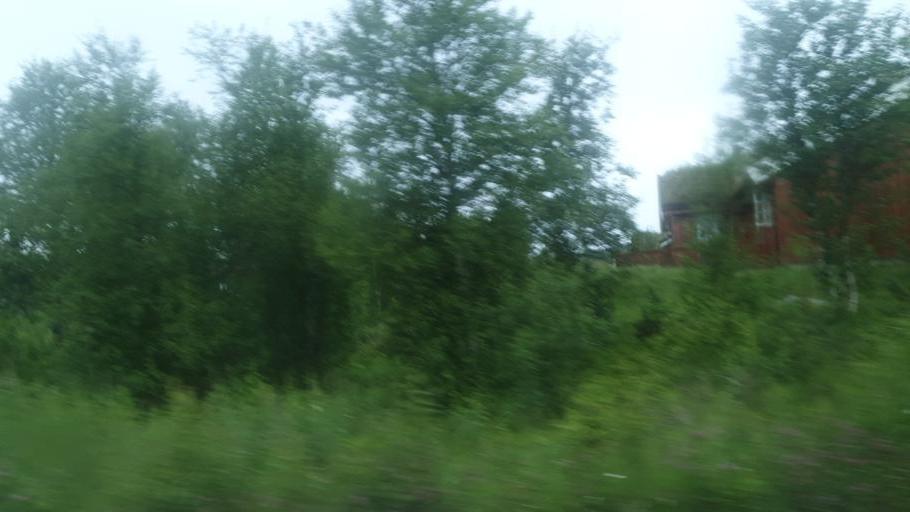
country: NO
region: Oppland
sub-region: Vestre Slidre
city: Slidre
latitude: 61.2400
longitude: 8.9173
